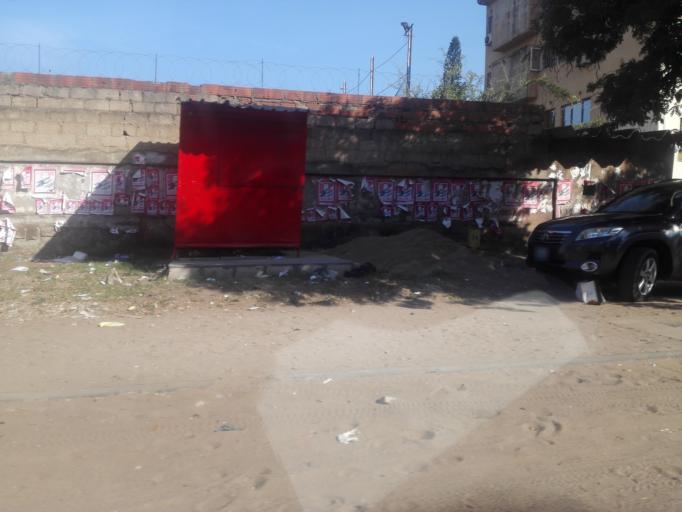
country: MZ
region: Maputo City
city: Maputo
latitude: -25.9587
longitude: 32.5846
